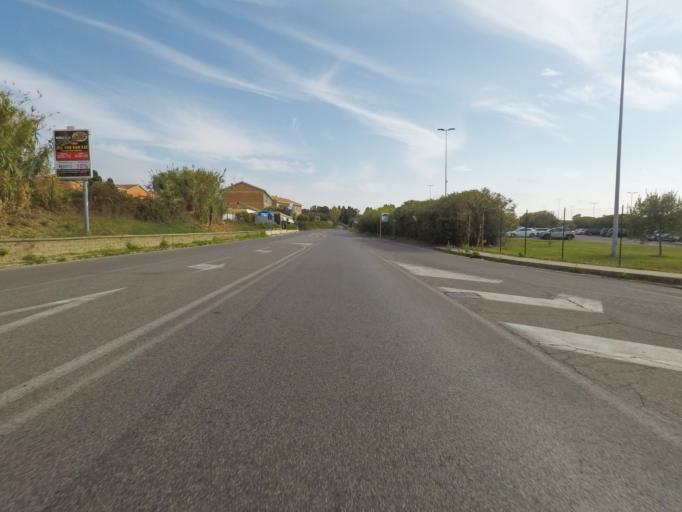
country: IT
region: Latium
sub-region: Citta metropolitana di Roma Capitale
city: Civitavecchia
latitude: 42.0616
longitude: 11.8160
